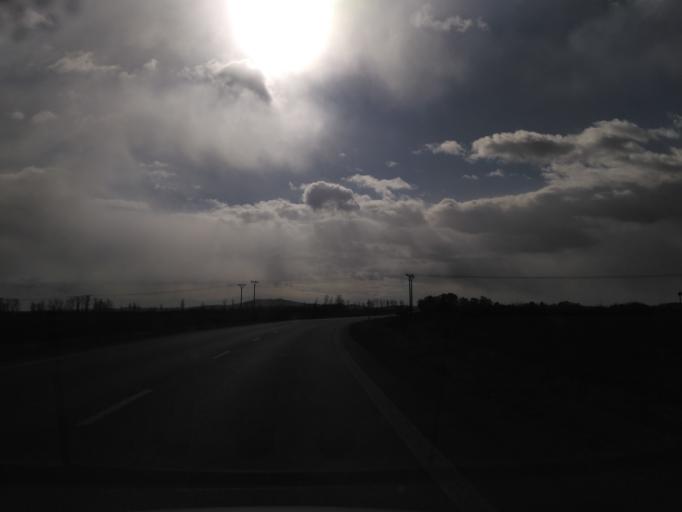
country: SK
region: Kosicky
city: Trebisov
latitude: 48.5984
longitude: 21.7138
